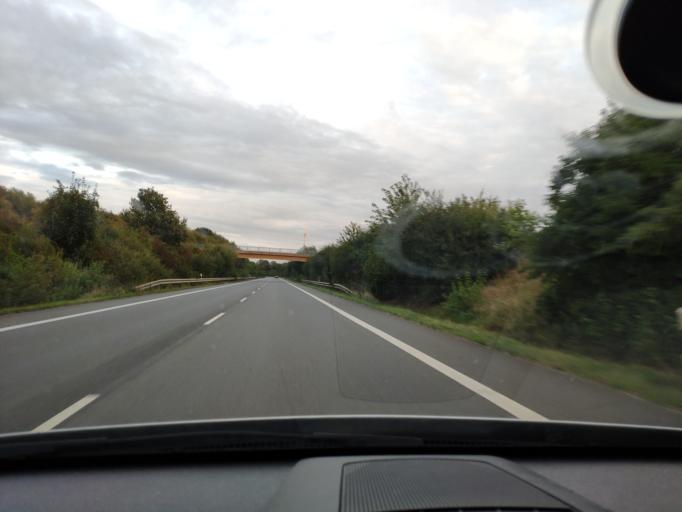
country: DE
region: North Rhine-Westphalia
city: Baesweiler
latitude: 50.9353
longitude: 6.2030
